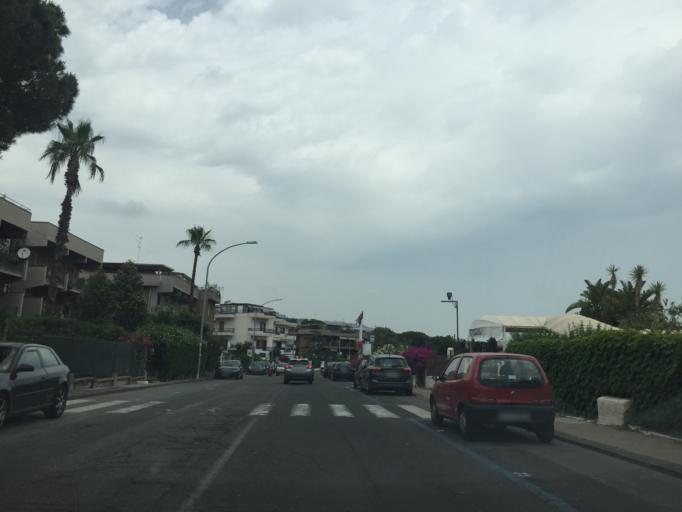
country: IT
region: Sicily
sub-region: Catania
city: Aci Castello
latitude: 37.5393
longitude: 15.1315
